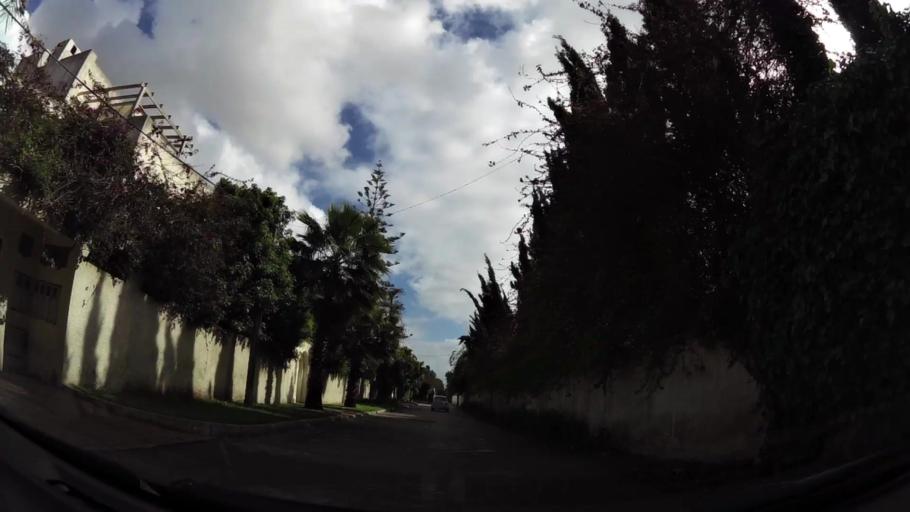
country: MA
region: Grand Casablanca
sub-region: Casablanca
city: Casablanca
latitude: 33.5485
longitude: -7.6249
